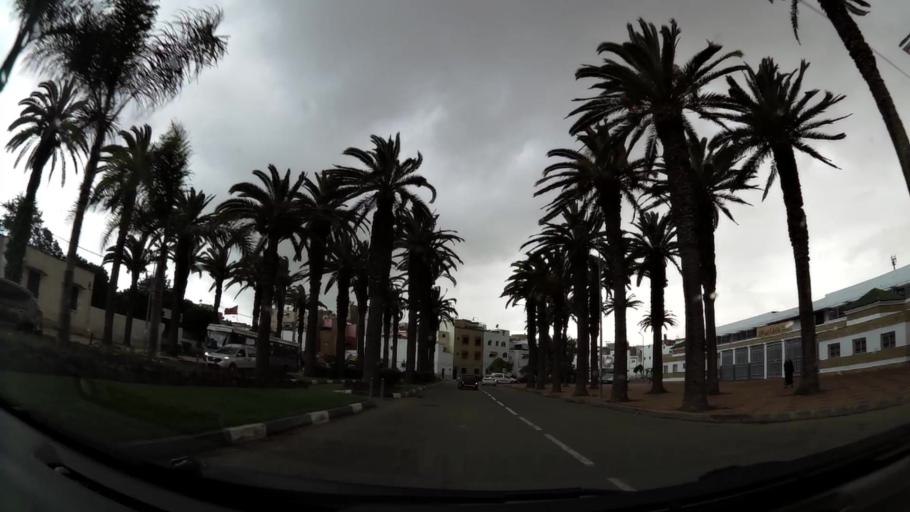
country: MA
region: Grand Casablanca
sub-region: Casablanca
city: Casablanca
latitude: 33.5553
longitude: -7.5949
